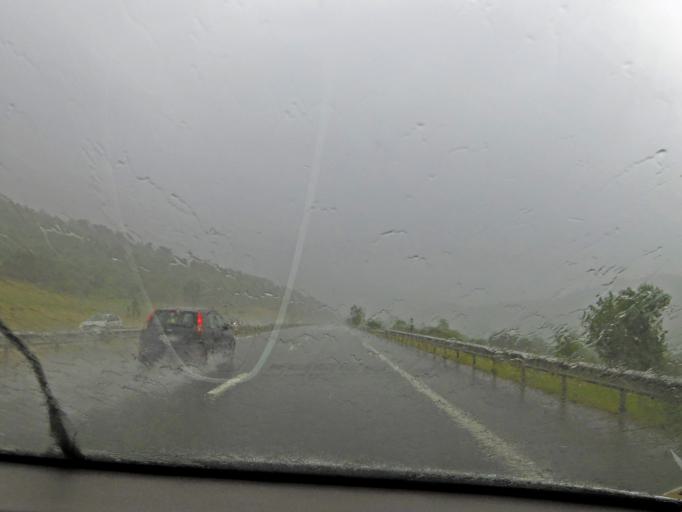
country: FR
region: Auvergne
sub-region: Departement du Cantal
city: Massiac
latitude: 45.2548
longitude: 3.2035
